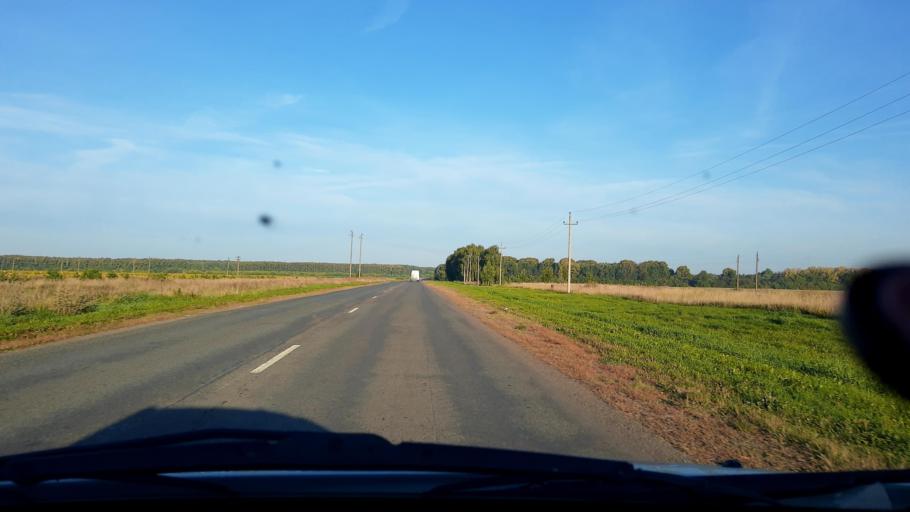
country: RU
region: Bashkortostan
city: Ulukulevo
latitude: 54.3744
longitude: 56.4069
